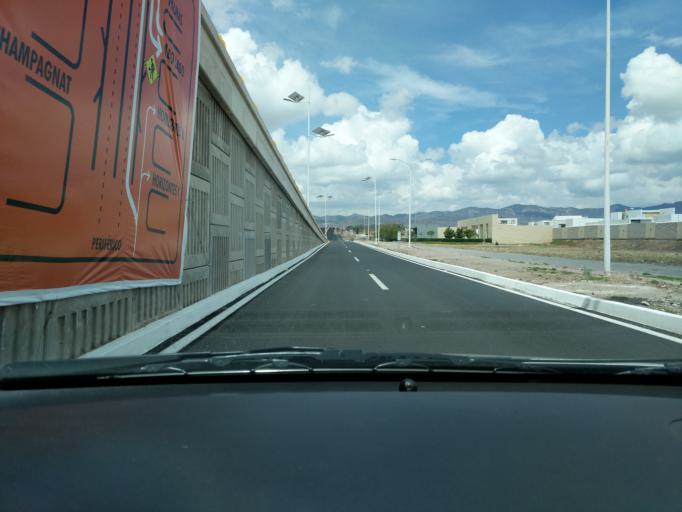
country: MX
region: San Luis Potosi
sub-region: Mexquitic de Carmona
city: Guadalupe Victoria
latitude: 22.1670
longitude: -101.0491
